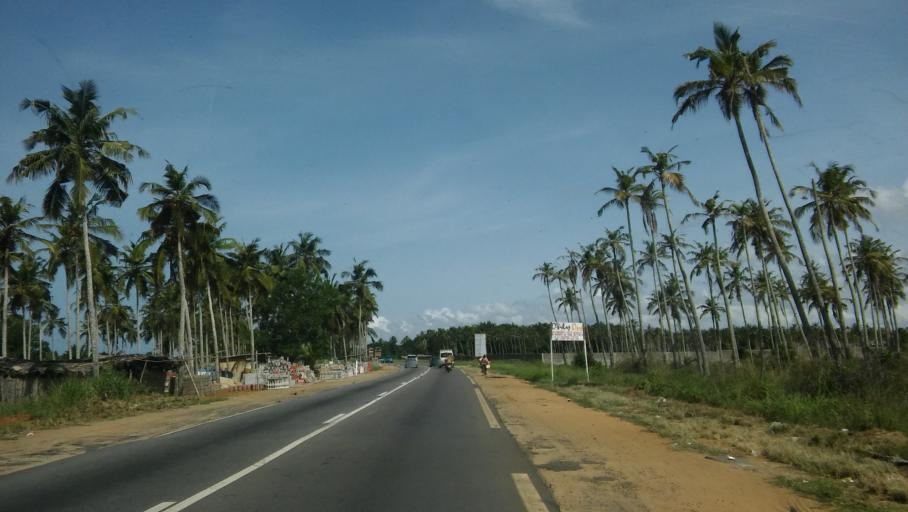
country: CI
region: Sud-Comoe
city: Grand-Bassam
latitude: 5.2148
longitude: -3.7905
